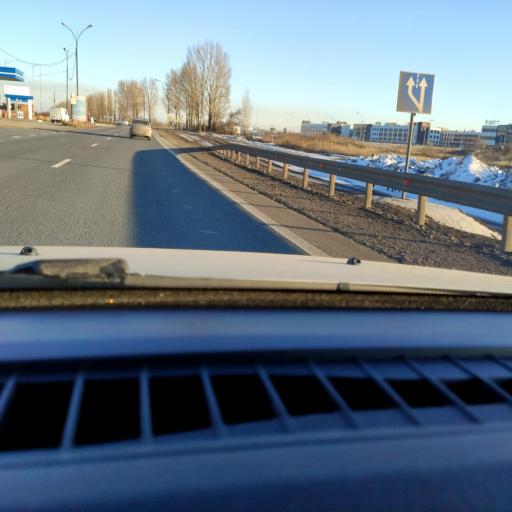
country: RU
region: Samara
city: Podstepki
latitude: 53.5598
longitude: 49.2118
